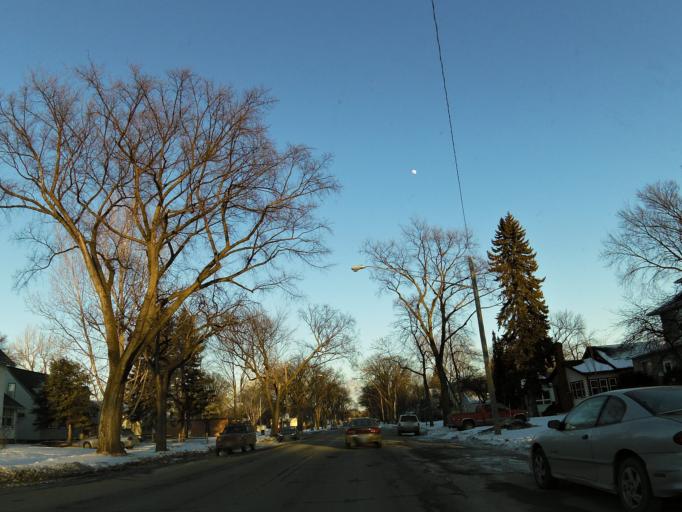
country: US
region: North Dakota
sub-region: Grand Forks County
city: Grand Forks
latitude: 47.9222
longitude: -97.0520
